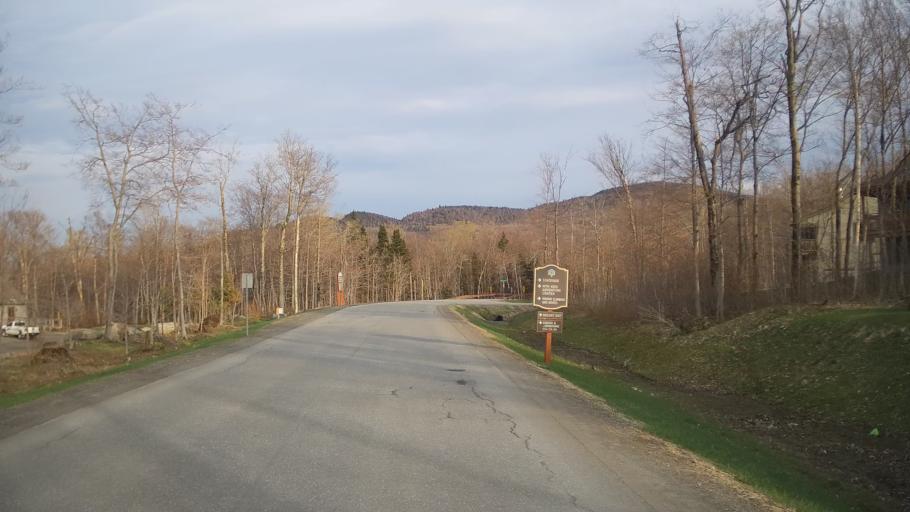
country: US
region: Vermont
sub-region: Franklin County
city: Richford
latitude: 44.9334
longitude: -72.4979
